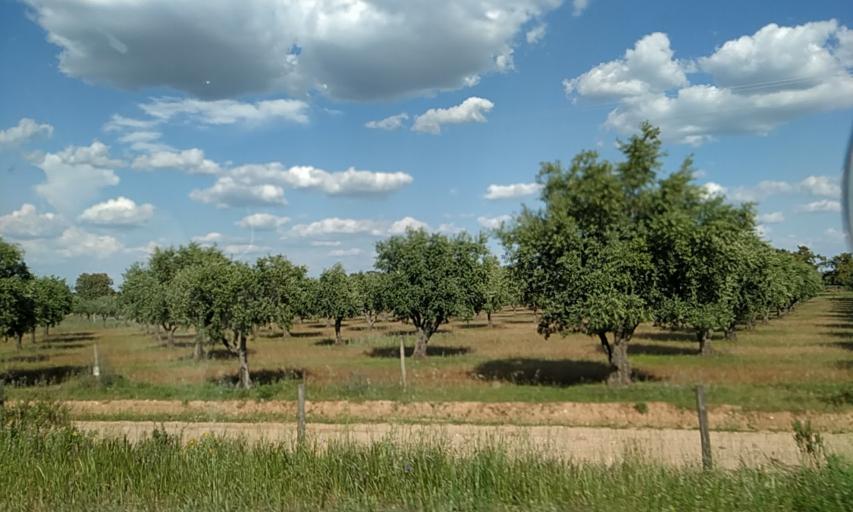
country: PT
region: Evora
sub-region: Estremoz
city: Estremoz
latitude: 38.8854
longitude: -7.5578
